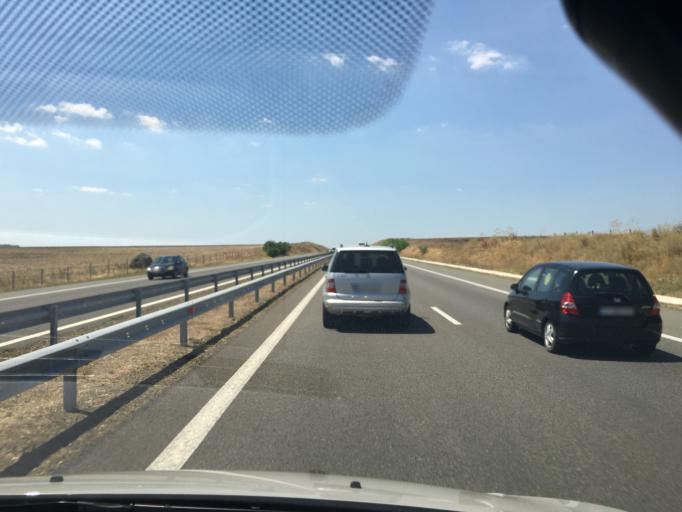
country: BG
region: Burgas
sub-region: Obshtina Karnobat
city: Karnobat
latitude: 42.5890
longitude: 26.9640
